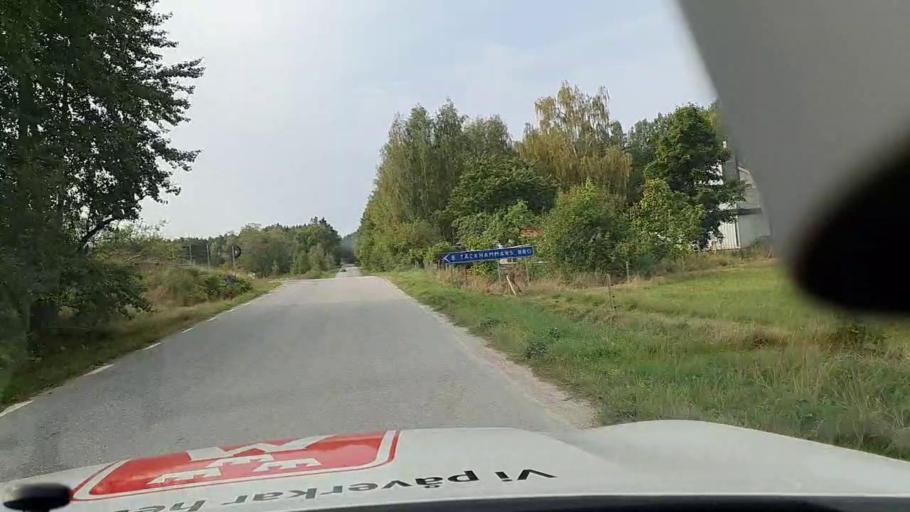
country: SE
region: Soedermanland
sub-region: Nykopings Kommun
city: Stigtomta
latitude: 58.8107
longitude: 16.8100
